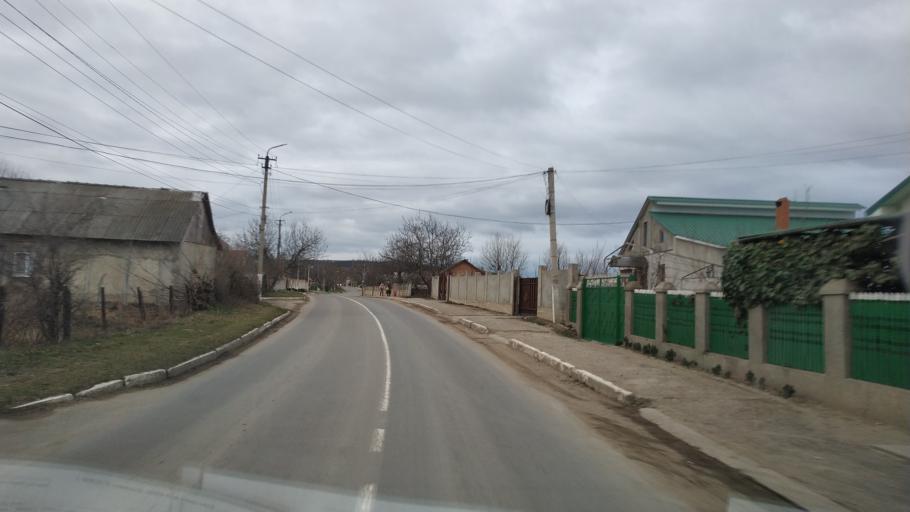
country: MD
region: Causeni
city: Causeni
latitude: 46.6457
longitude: 29.4215
